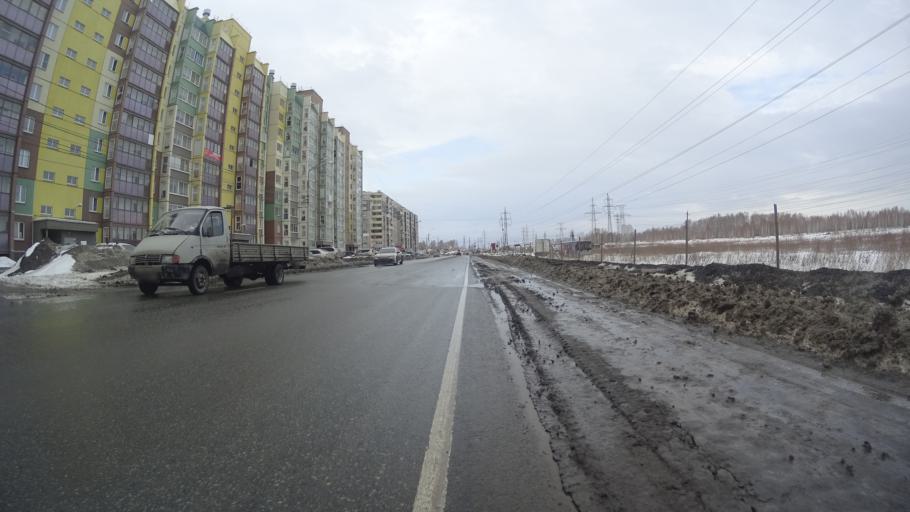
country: RU
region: Chelyabinsk
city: Roshchino
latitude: 55.2171
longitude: 61.3014
